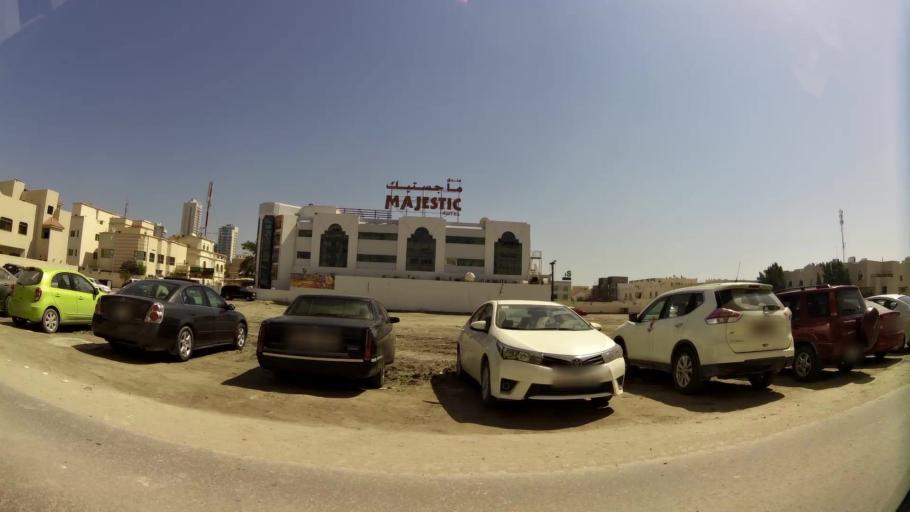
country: BH
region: Manama
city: Manama
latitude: 26.2117
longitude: 50.6123
